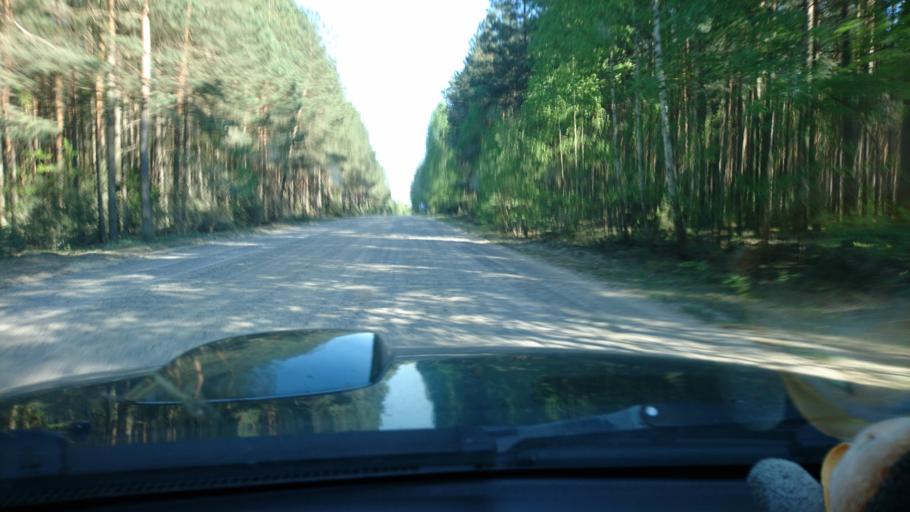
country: BY
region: Brest
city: Zhabinka
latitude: 52.3826
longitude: 24.1166
